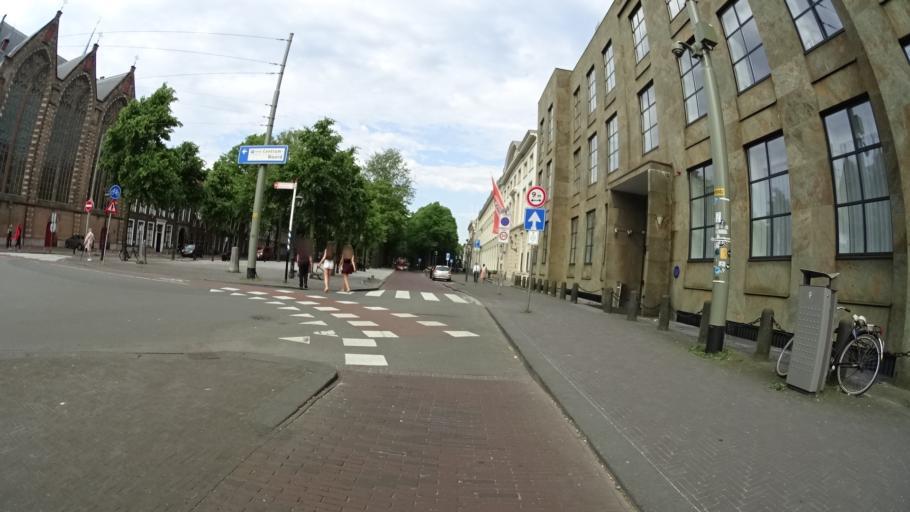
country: NL
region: South Holland
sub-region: Gemeente Den Haag
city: The Hague
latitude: 52.0813
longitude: 4.3094
